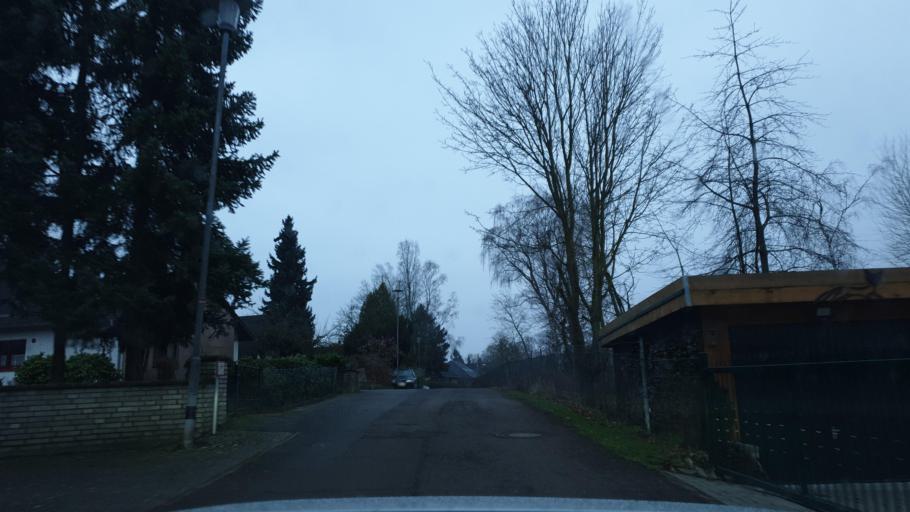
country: DE
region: North Rhine-Westphalia
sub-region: Regierungsbezirk Detmold
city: Petershagen
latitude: 52.3799
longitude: 8.9607
